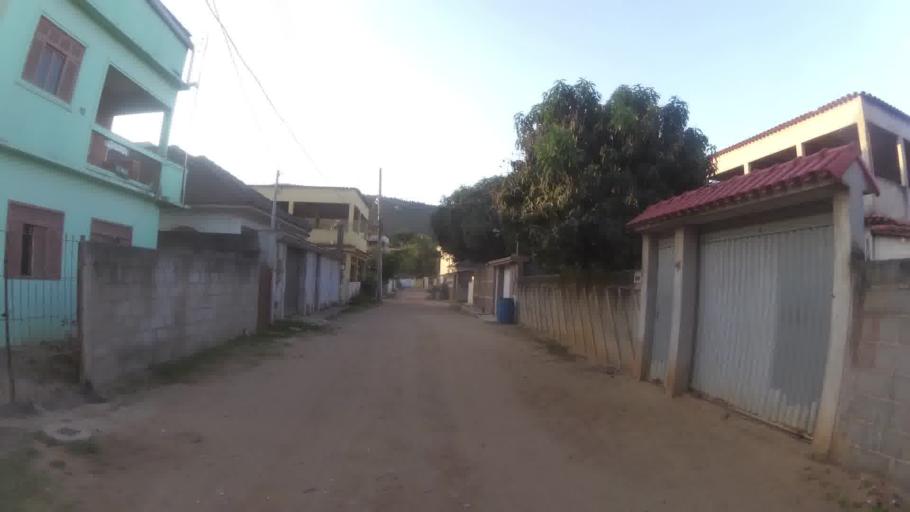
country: BR
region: Espirito Santo
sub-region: Piuma
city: Piuma
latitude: -20.8873
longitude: -40.7771
